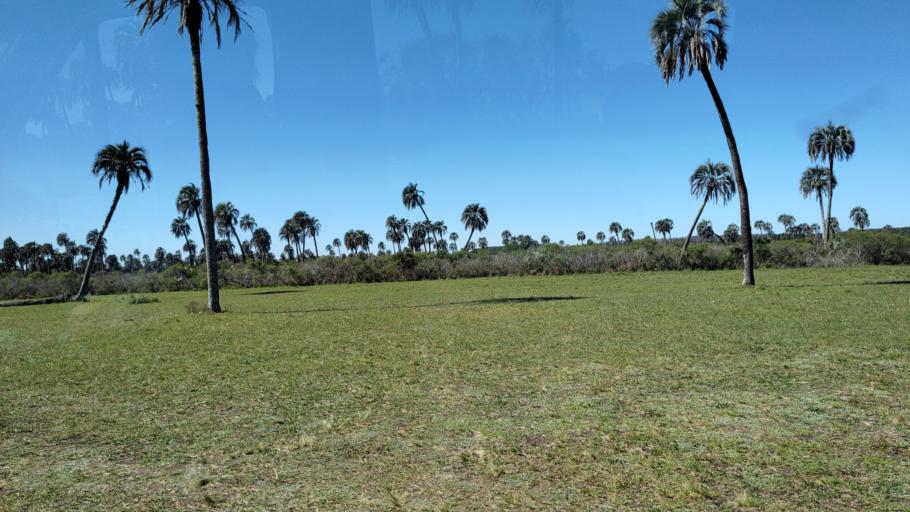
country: AR
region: Entre Rios
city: Ubajay
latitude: -31.8543
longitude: -58.3204
